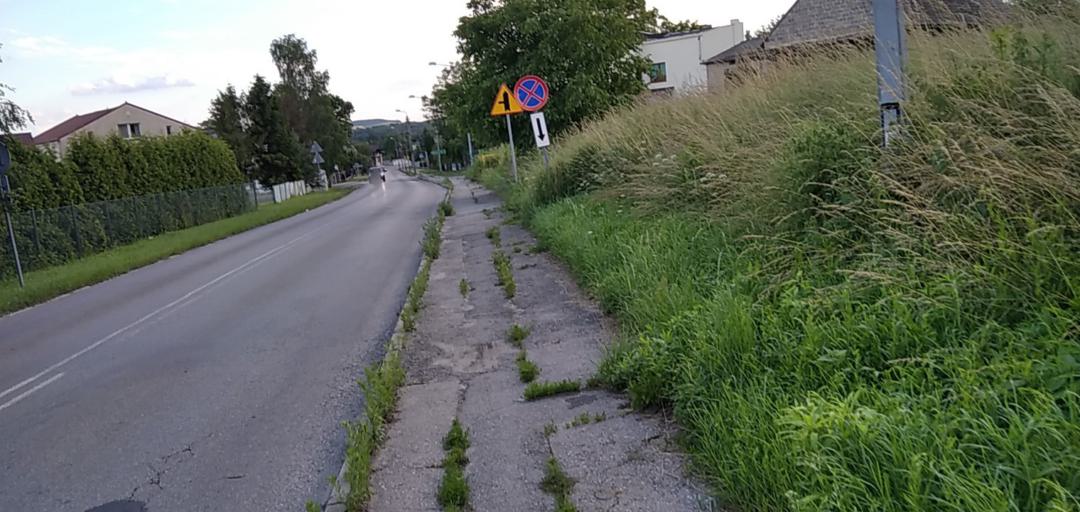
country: PL
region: Silesian Voivodeship
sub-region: Powiat bedzinski
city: Sarnow
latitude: 50.4080
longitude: 19.1396
